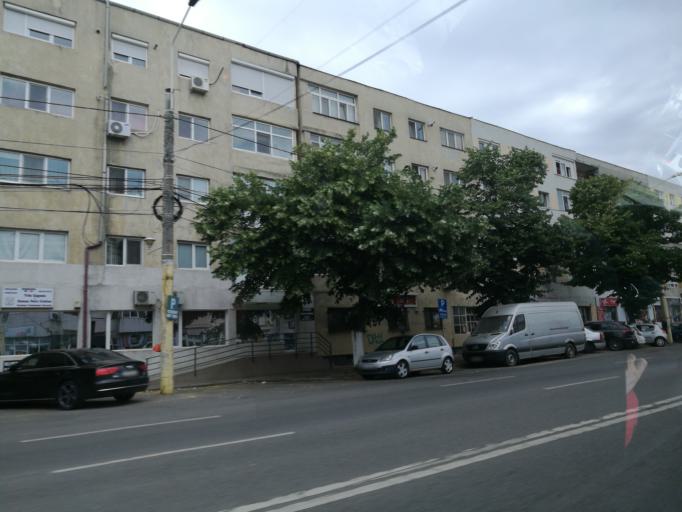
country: RO
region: Constanta
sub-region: Municipiul Constanta
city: Constanta
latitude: 44.1948
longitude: 28.6323
